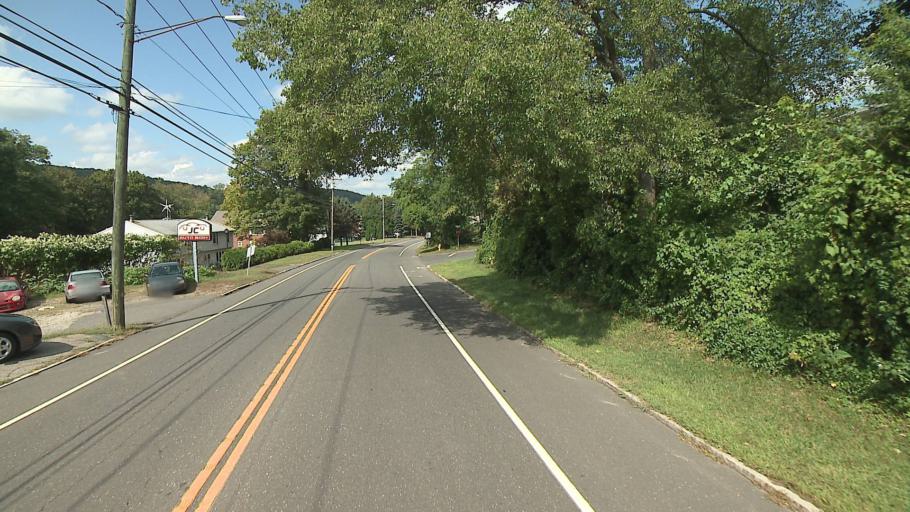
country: US
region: Connecticut
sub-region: New Haven County
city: Ansonia
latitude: 41.3680
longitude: -73.0828
